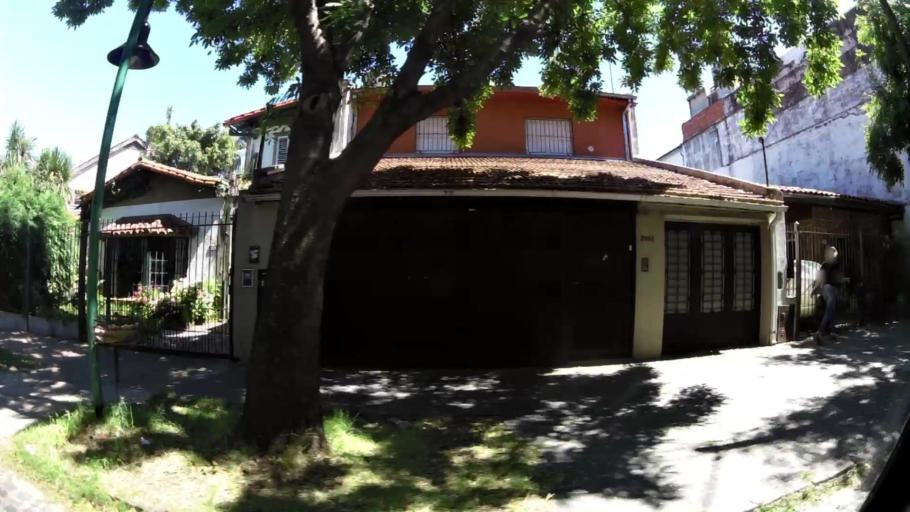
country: AR
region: Buenos Aires
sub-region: Partido de Vicente Lopez
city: Olivos
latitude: -34.5193
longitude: -58.5023
